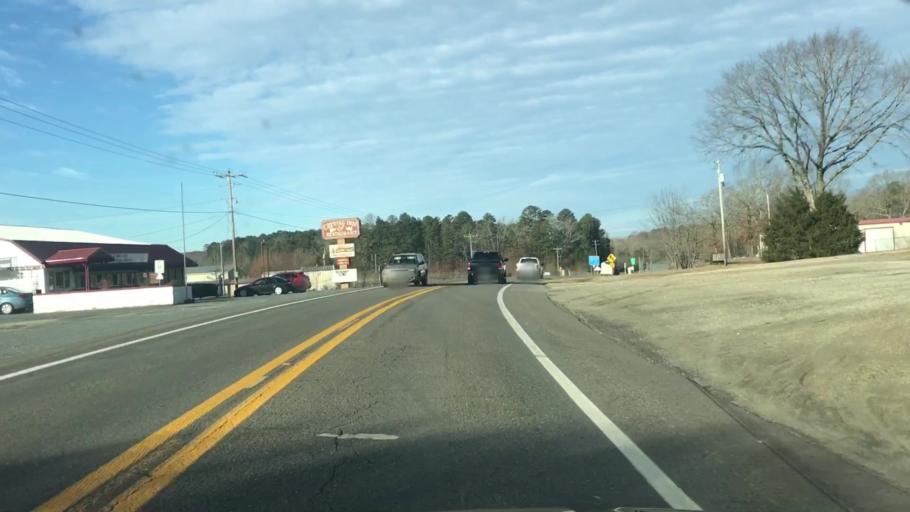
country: US
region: Arkansas
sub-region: Montgomery County
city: Mount Ida
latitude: 34.5309
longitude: -93.5292
